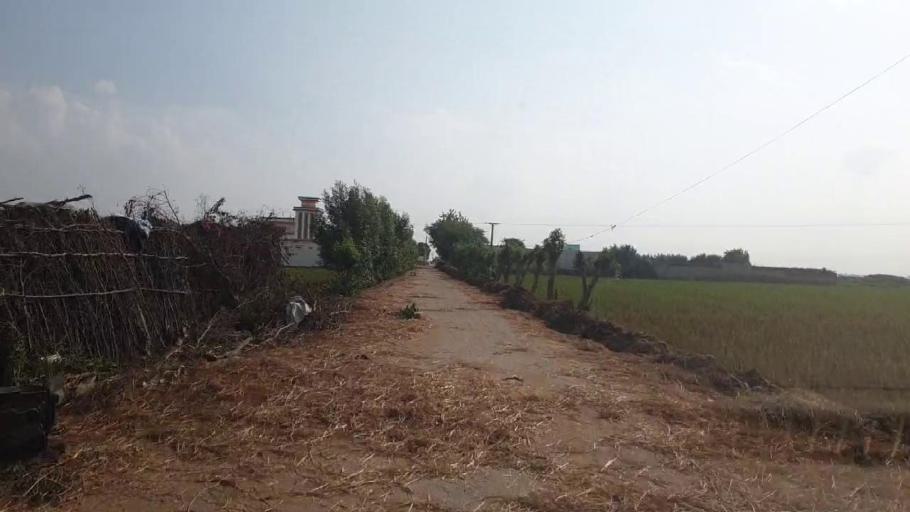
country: PK
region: Sindh
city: Kario
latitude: 24.6389
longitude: 68.5580
